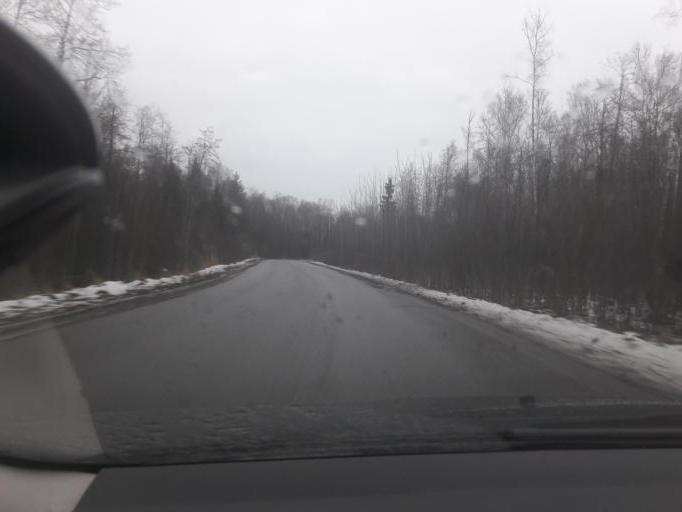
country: RU
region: Moskovskaya
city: Fryazevo
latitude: 55.7652
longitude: 38.5039
